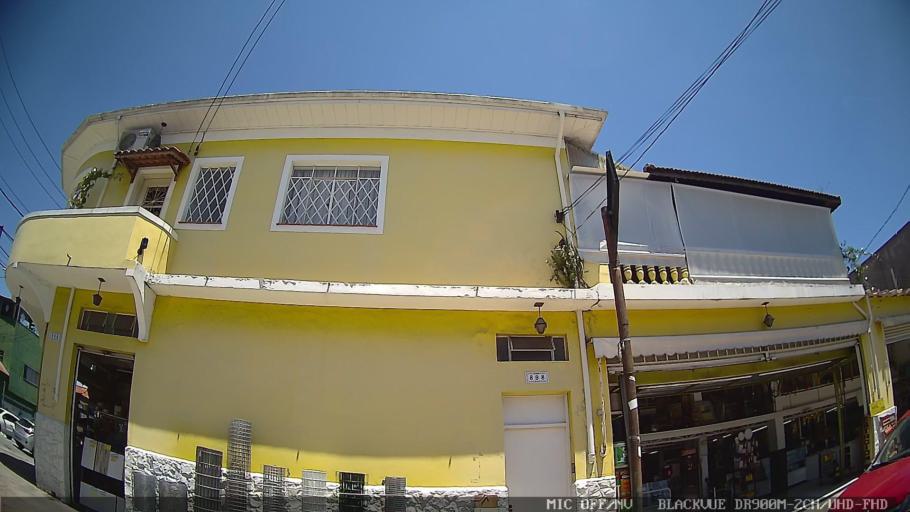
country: BR
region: Sao Paulo
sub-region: Sao Caetano Do Sul
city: Sao Caetano do Sul
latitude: -23.5963
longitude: -46.5716
